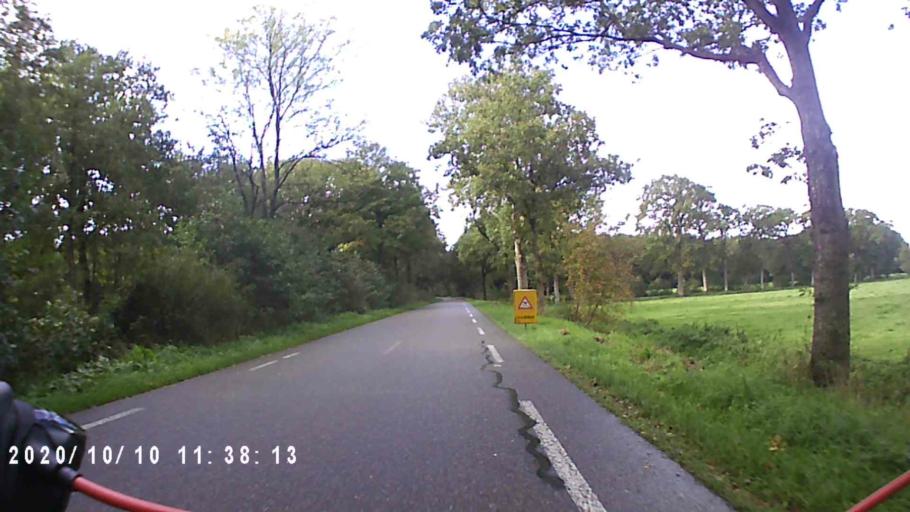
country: NL
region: Friesland
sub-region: Gemeente Smallingerland
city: Drachten
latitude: 53.0717
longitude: 6.1111
